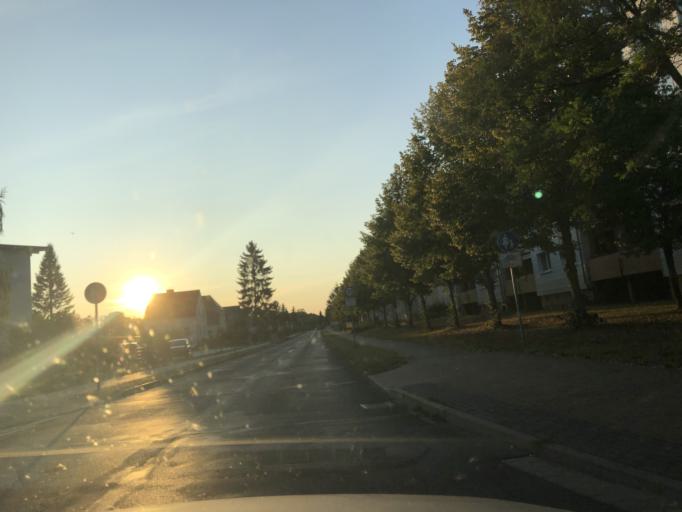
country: DE
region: Brandenburg
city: Mullrose
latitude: 52.2538
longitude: 14.4270
